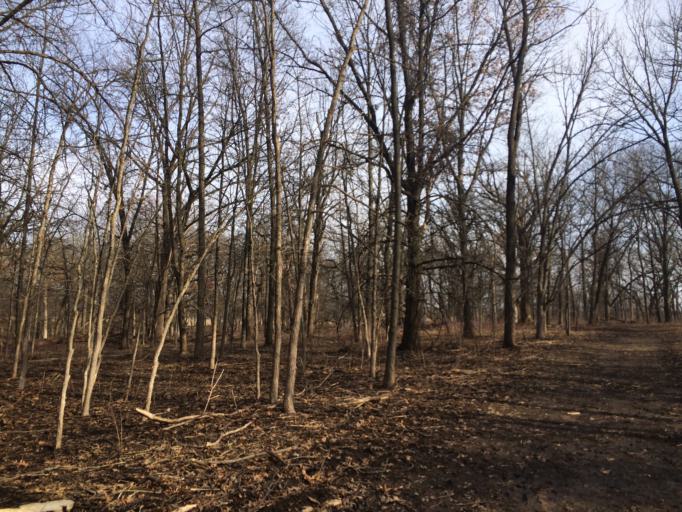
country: US
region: Illinois
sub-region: Cook County
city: Streamwood
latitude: 42.0516
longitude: -88.1989
